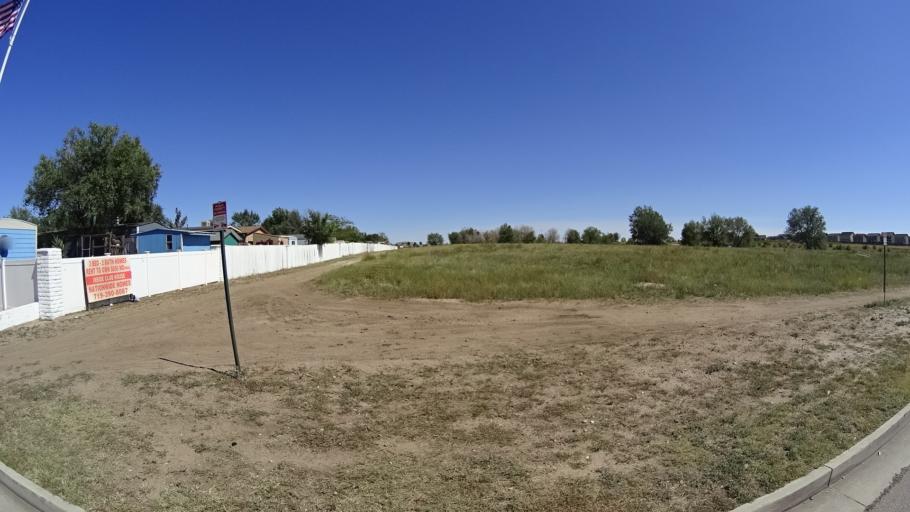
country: US
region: Colorado
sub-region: El Paso County
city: Security-Widefield
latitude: 38.7902
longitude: -104.7334
